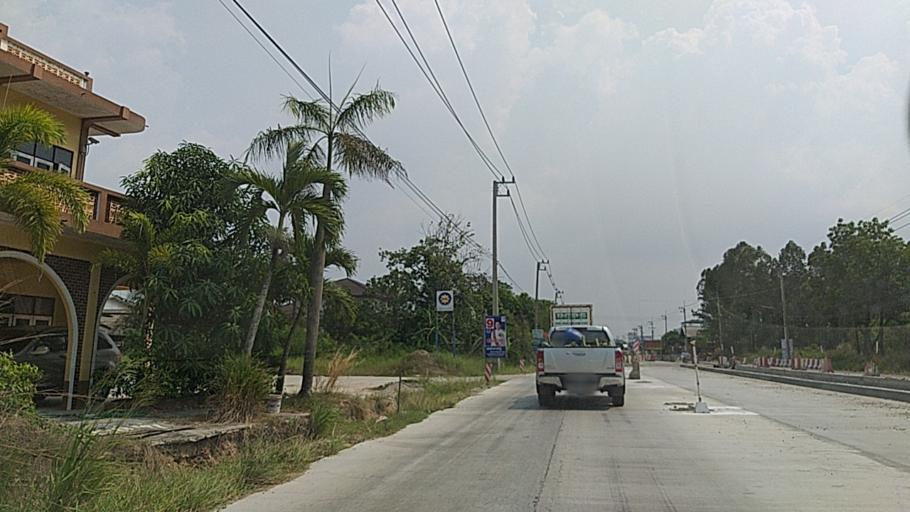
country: TH
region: Chon Buri
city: Phanat Nikhom
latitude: 13.3760
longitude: 101.1948
